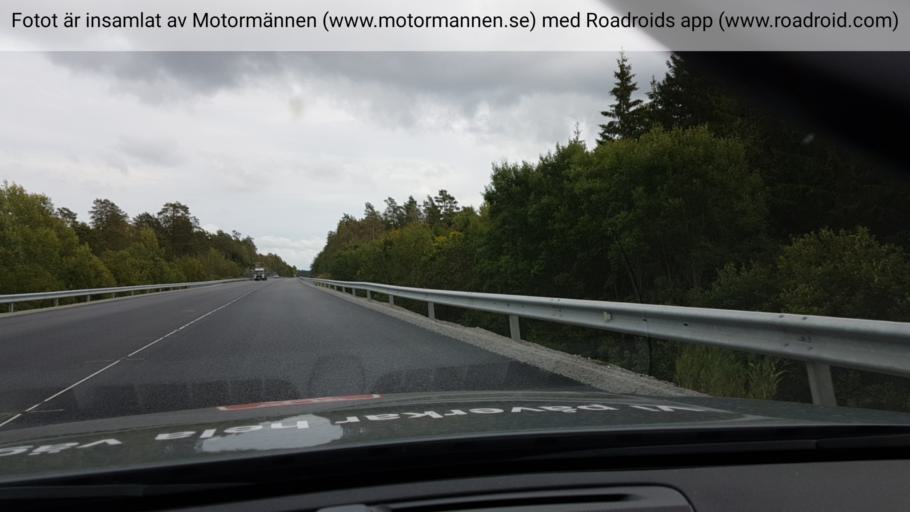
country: SE
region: Stockholm
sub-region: Norrtalje Kommun
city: Norrtalje
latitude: 59.7356
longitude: 18.7711
